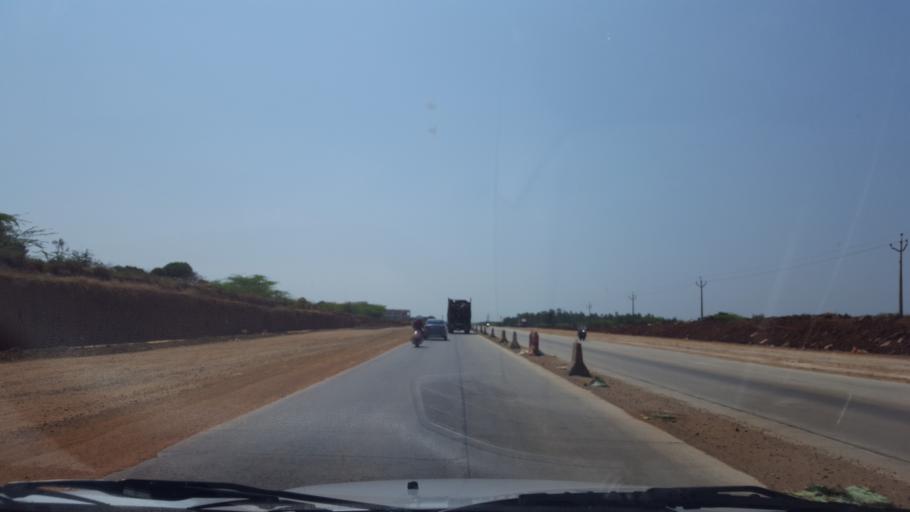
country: IN
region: Andhra Pradesh
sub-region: Prakasam
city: Singarayakonda
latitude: 15.2578
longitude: 80.0123
